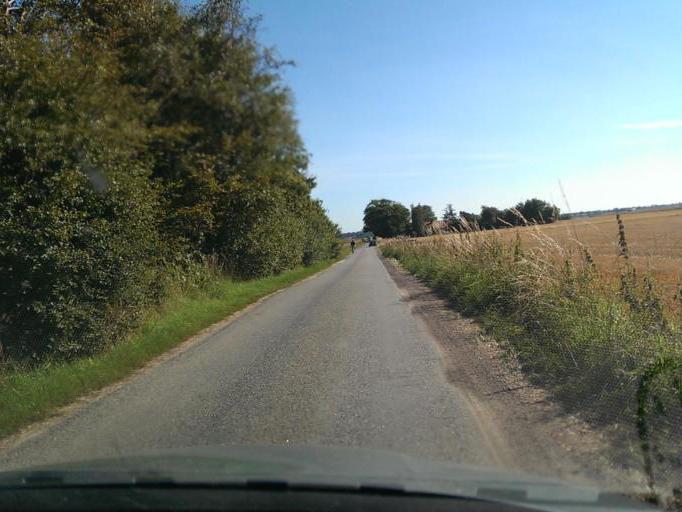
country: DK
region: Central Jutland
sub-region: Hedensted Kommune
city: Juelsminde
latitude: 55.8496
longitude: 10.0475
